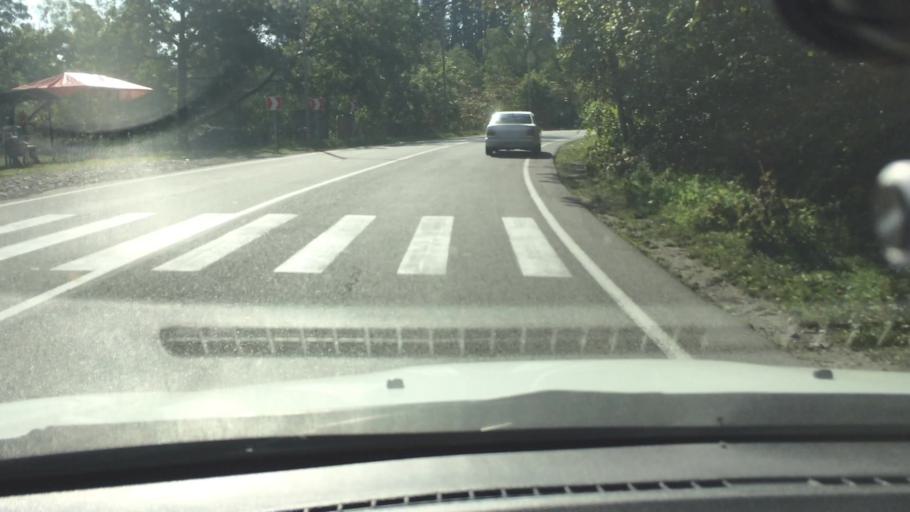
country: GE
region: Guria
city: Urek'i
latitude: 41.9860
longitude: 41.7839
